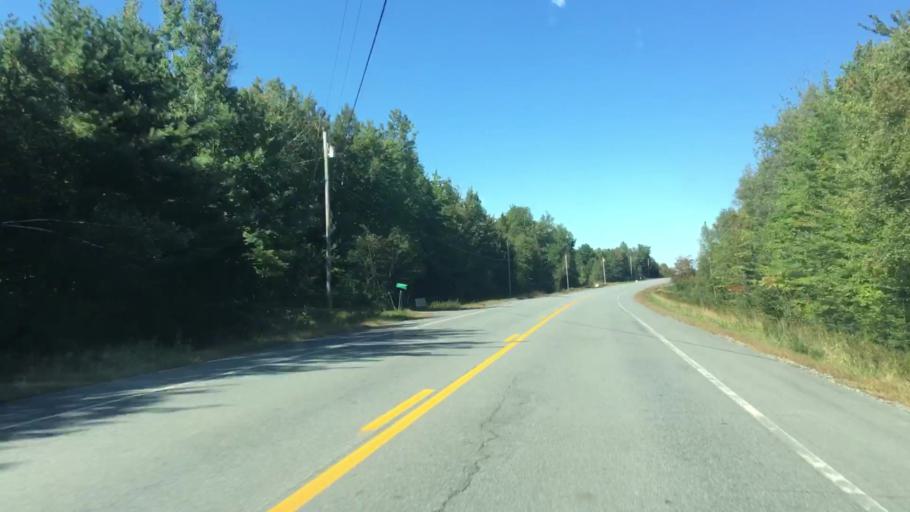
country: US
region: Maine
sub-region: Piscataquis County
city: Sangerville
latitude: 45.0684
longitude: -69.4588
